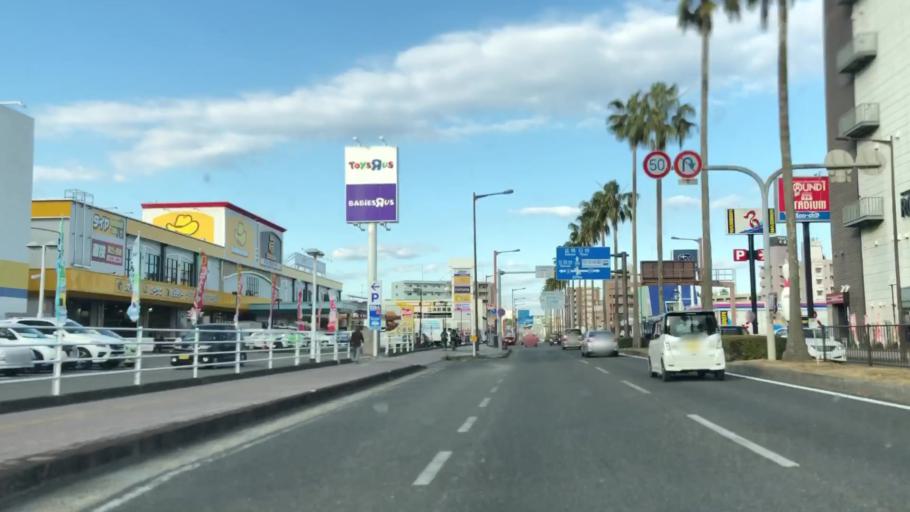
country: JP
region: Miyazaki
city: Miyazaki-shi
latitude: 31.8951
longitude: 131.4169
